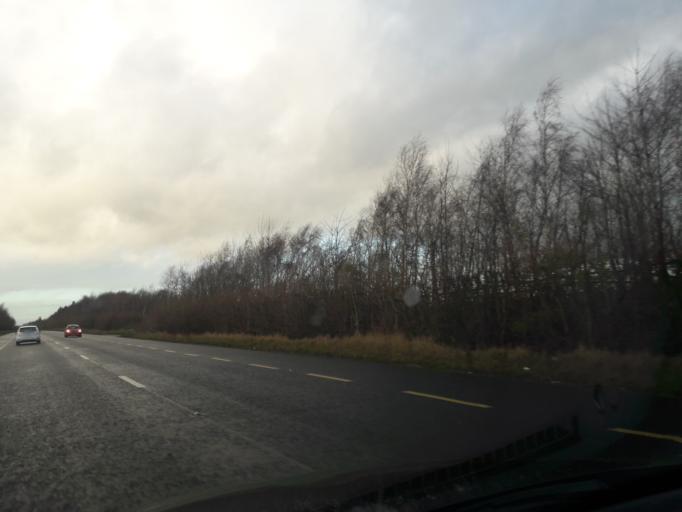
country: IE
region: Leinster
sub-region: Lu
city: Ardee
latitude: 53.8968
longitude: -6.5876
